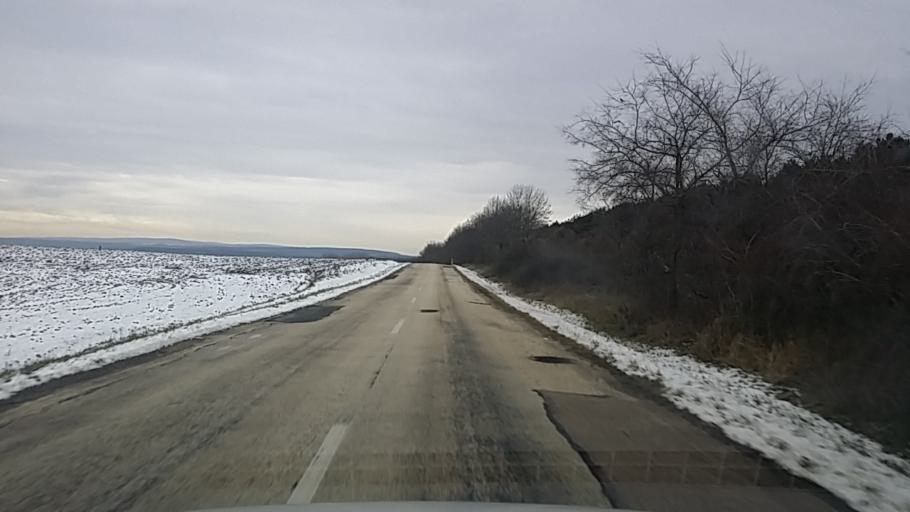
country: HU
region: Fejer
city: Fehervarcsurgo
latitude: 47.3265
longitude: 18.2990
